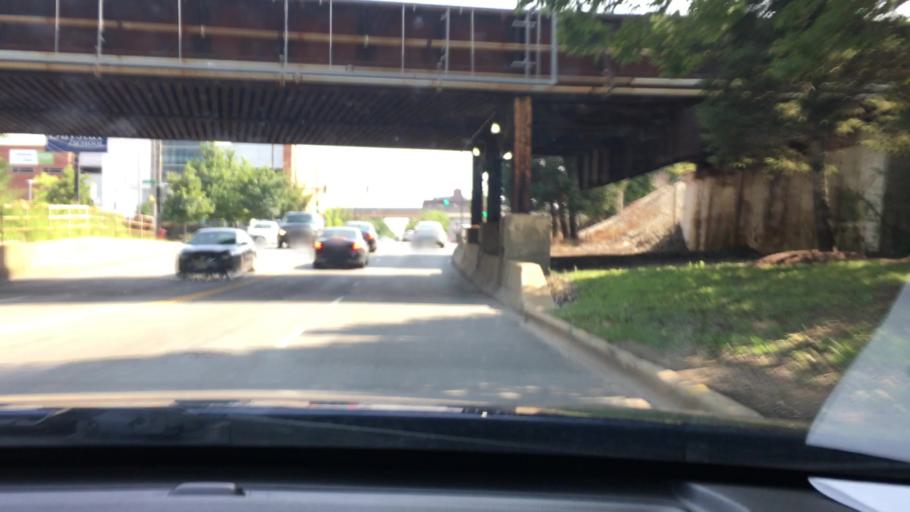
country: US
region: Illinois
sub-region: Cook County
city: Chicago
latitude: 41.8606
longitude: -87.6303
